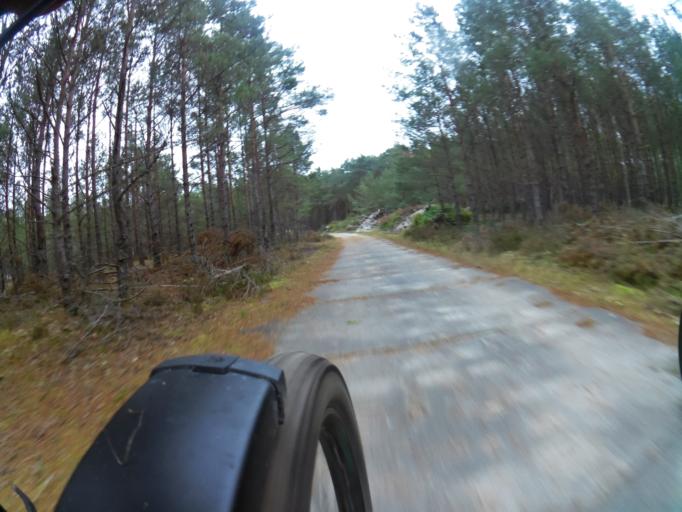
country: PL
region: Pomeranian Voivodeship
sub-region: Powiat wejherowski
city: Choczewo
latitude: 54.7810
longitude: 17.7299
